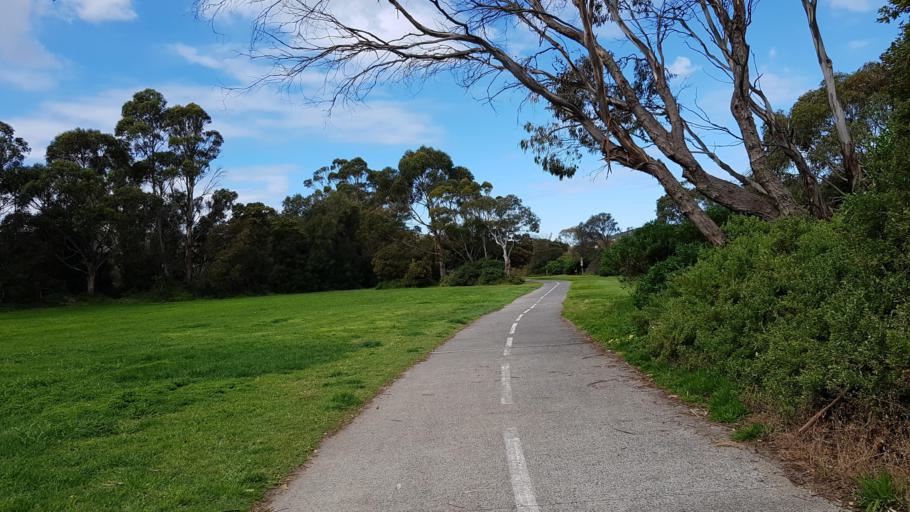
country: AU
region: Tasmania
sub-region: Clarence
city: Howrah
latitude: -42.8806
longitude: 147.3933
